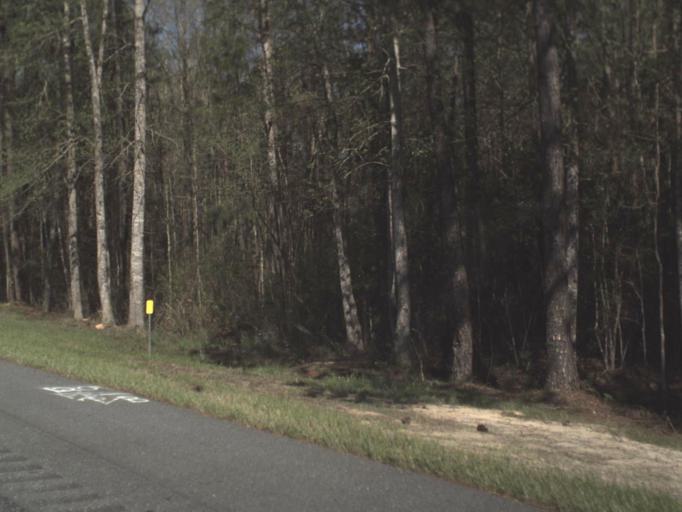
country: US
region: Florida
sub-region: Walton County
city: DeFuniak Springs
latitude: 30.6907
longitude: -86.0384
